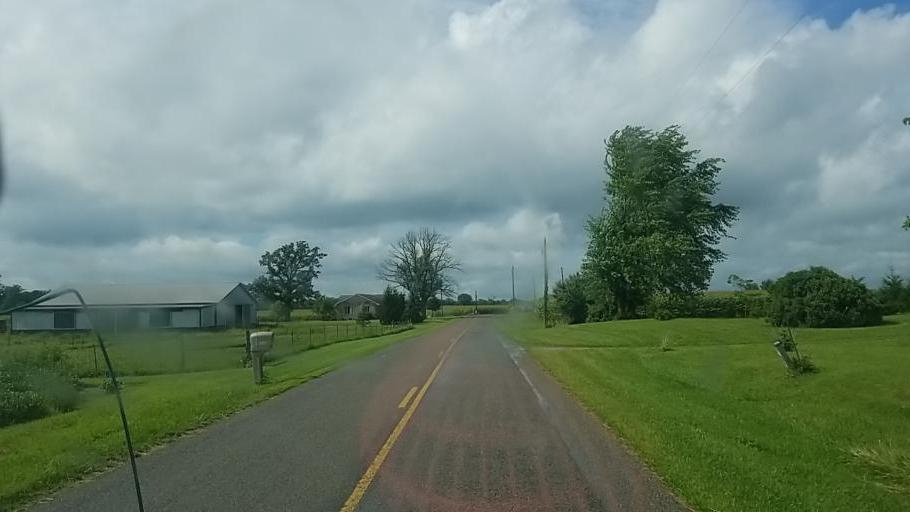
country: US
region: Ohio
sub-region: Hardin County
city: Kenton
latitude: 40.4914
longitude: -83.5178
